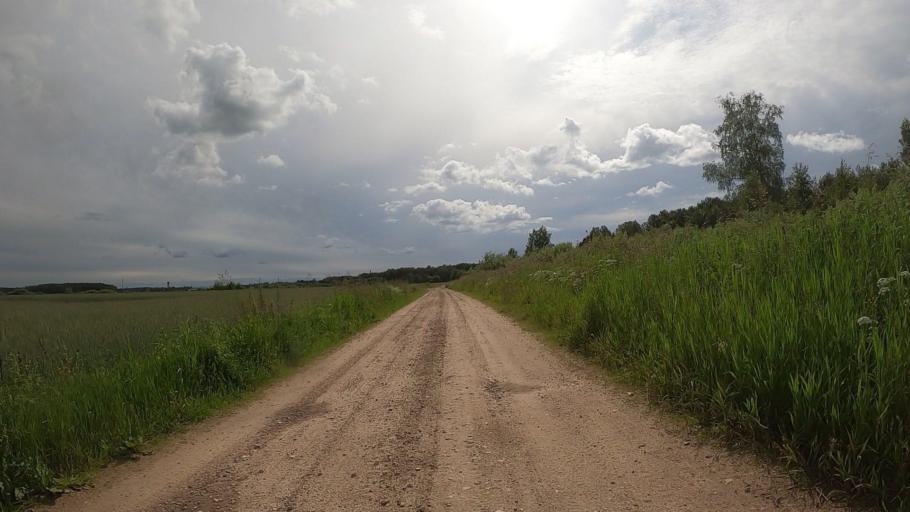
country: LV
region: Olaine
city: Olaine
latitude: 56.8157
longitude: 23.9349
